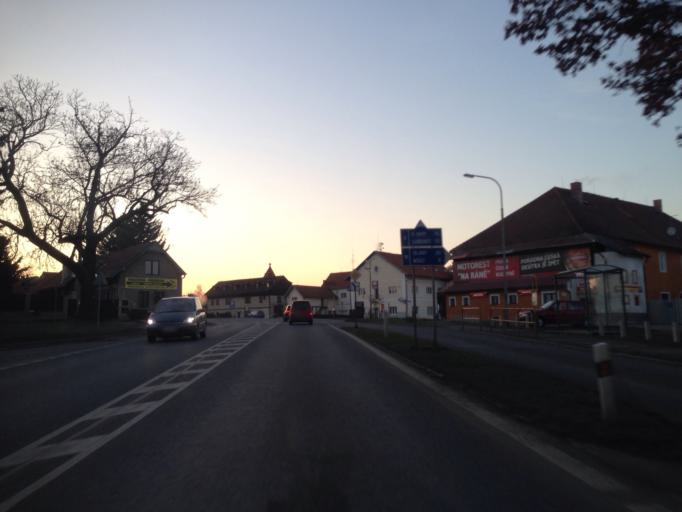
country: CZ
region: Central Bohemia
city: Revnicov
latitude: 50.1830
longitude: 13.8090
